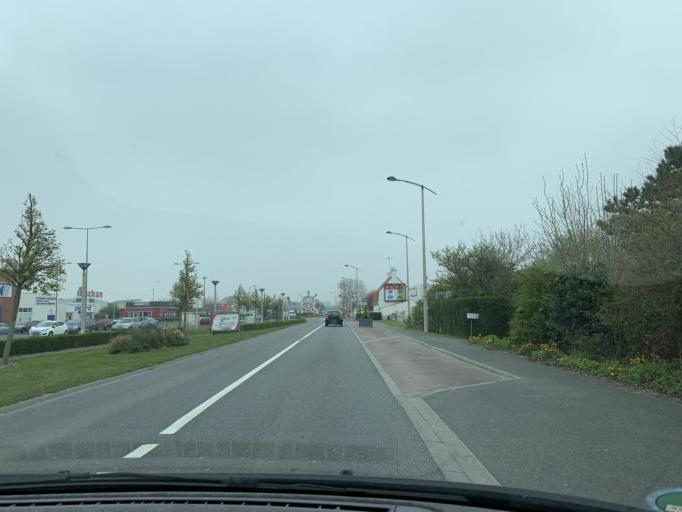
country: FR
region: Nord-Pas-de-Calais
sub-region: Departement du Pas-de-Calais
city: Coquelles
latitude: 50.9420
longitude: 1.8061
